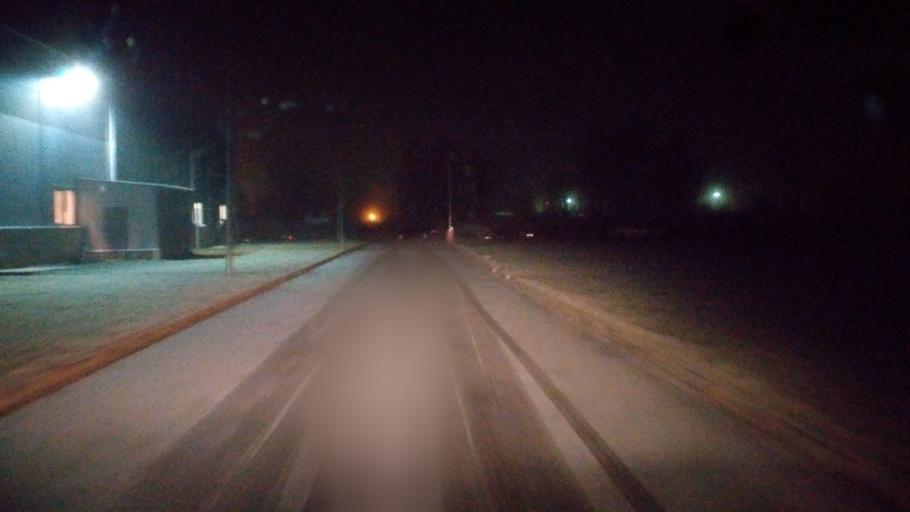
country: LV
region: Olaine
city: Olaine
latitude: 56.8025
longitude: 23.9299
